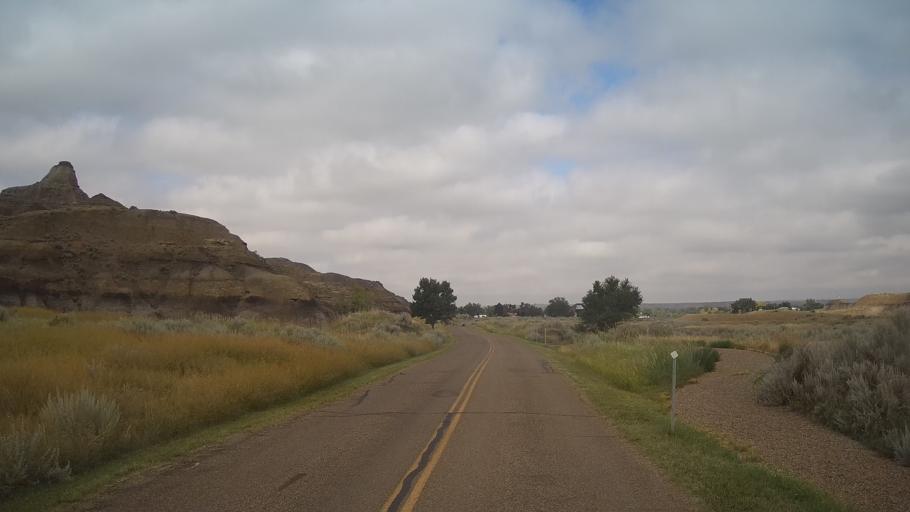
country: US
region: Montana
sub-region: Dawson County
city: Glendive
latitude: 47.0868
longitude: -104.7009
